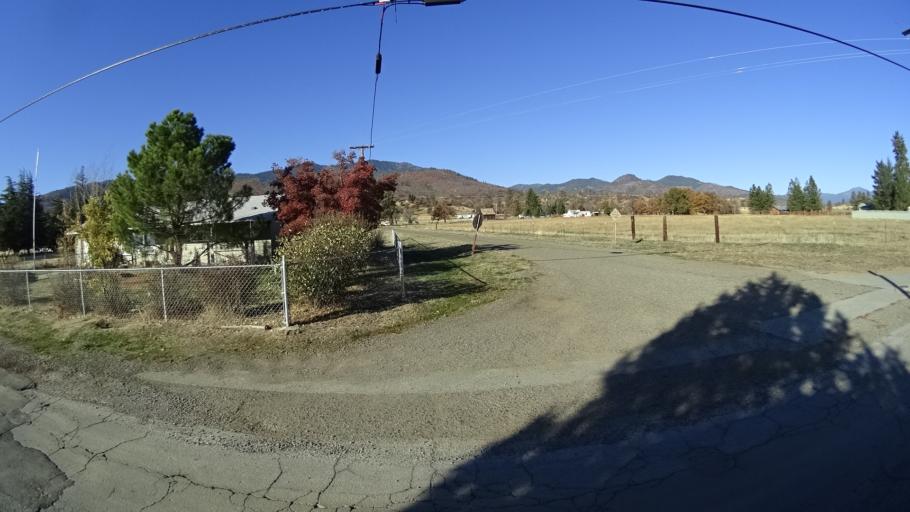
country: US
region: California
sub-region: Siskiyou County
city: Montague
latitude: 41.9075
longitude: -122.5631
